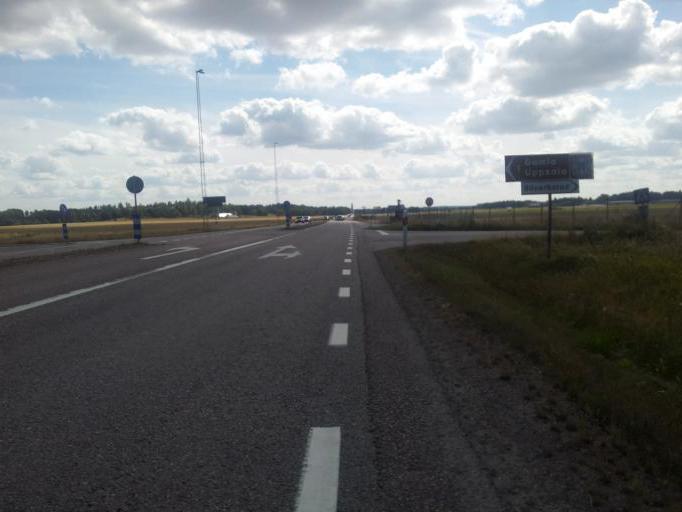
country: SE
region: Uppsala
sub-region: Uppsala Kommun
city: Gamla Uppsala
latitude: 59.9049
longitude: 17.6100
